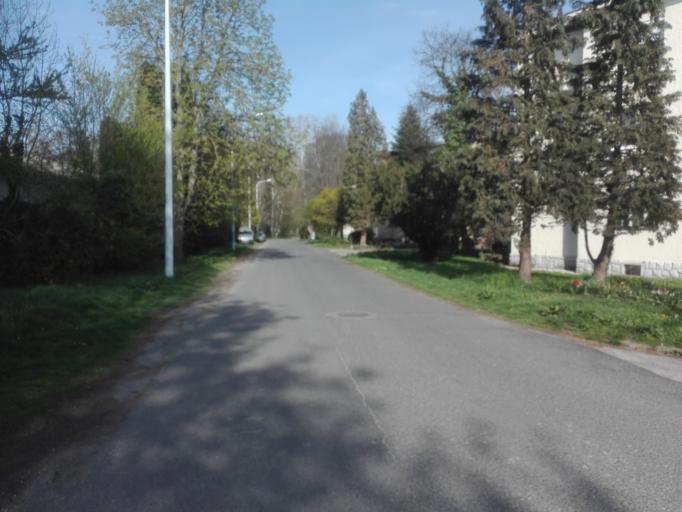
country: HU
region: Vas
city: Kormend
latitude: 47.0085
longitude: 16.6080
